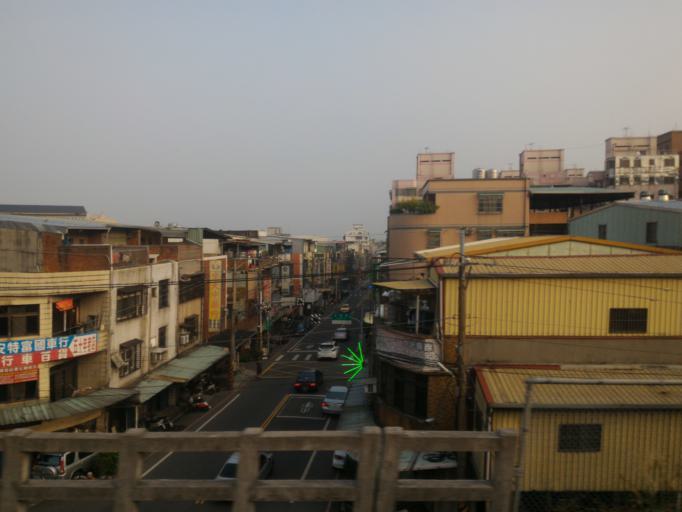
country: TW
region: Taiwan
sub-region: Taoyuan
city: Taoyuan
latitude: 24.9556
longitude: 121.3368
